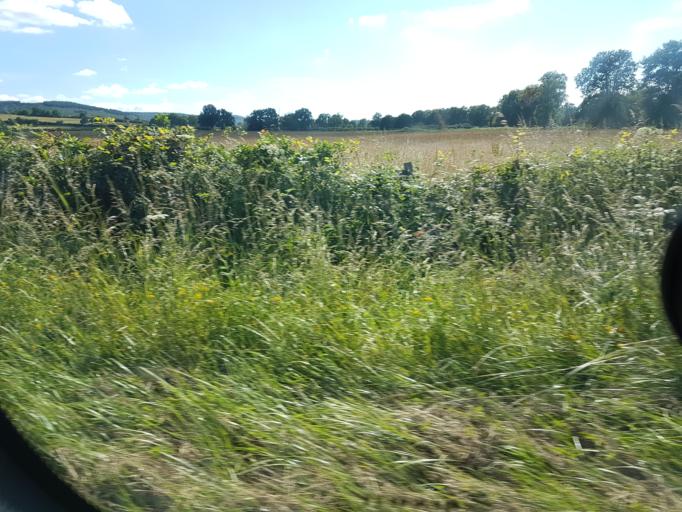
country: FR
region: Bourgogne
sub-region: Departement de Saone-et-Loire
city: Epinac
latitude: 47.0013
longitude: 4.4773
